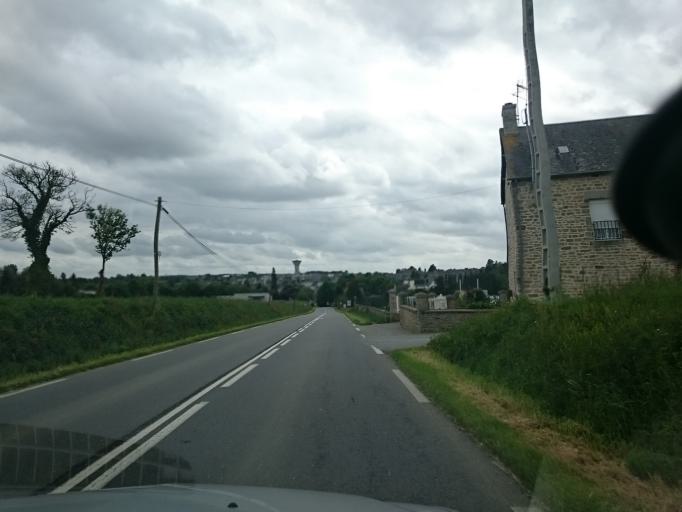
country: FR
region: Brittany
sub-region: Departement d'Ille-et-Vilaine
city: Antrain
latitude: 48.4667
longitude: -1.4774
